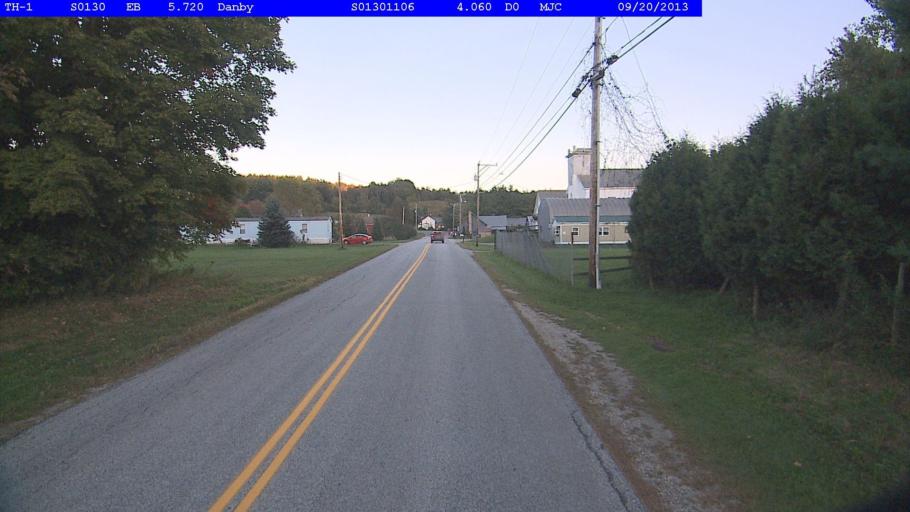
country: US
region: Vermont
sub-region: Bennington County
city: Manchester Center
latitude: 43.3553
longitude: -73.0505
